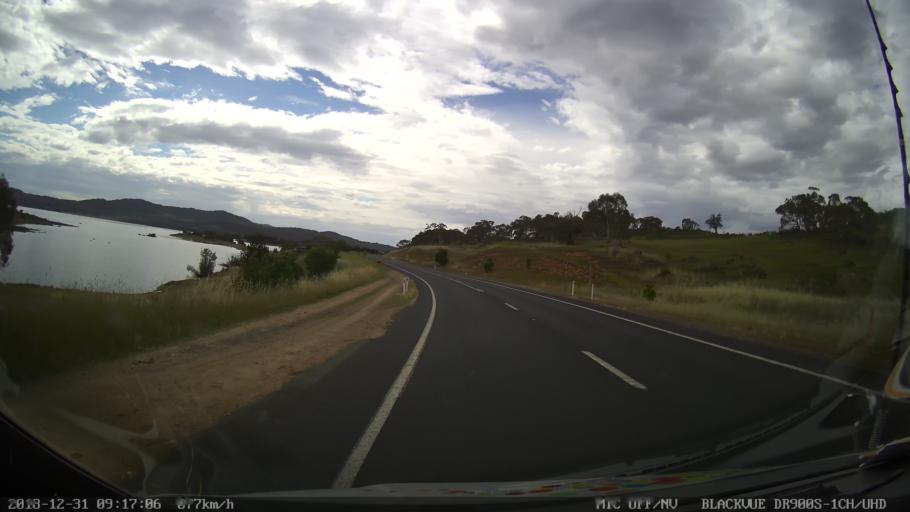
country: AU
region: New South Wales
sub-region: Snowy River
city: Jindabyne
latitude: -36.4035
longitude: 148.5975
